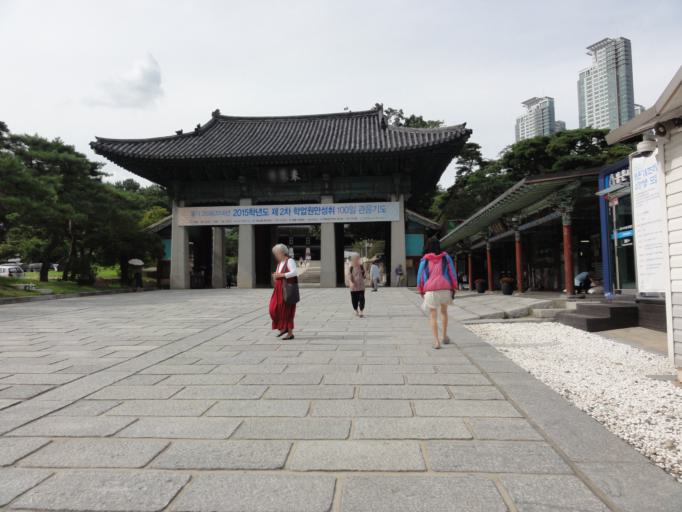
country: KR
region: Seoul
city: Seoul
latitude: 37.5139
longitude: 127.0583
